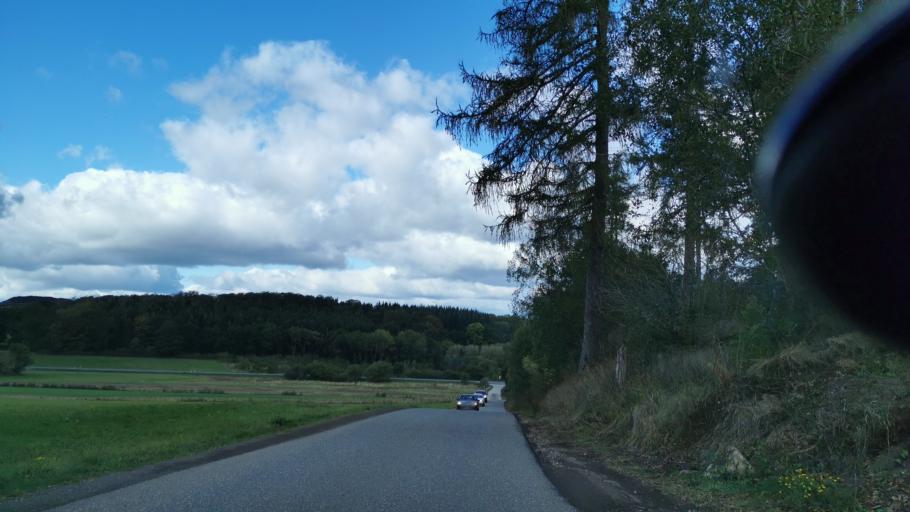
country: DE
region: Rheinland-Pfalz
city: Walsdorf
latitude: 50.2780
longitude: 6.7027
